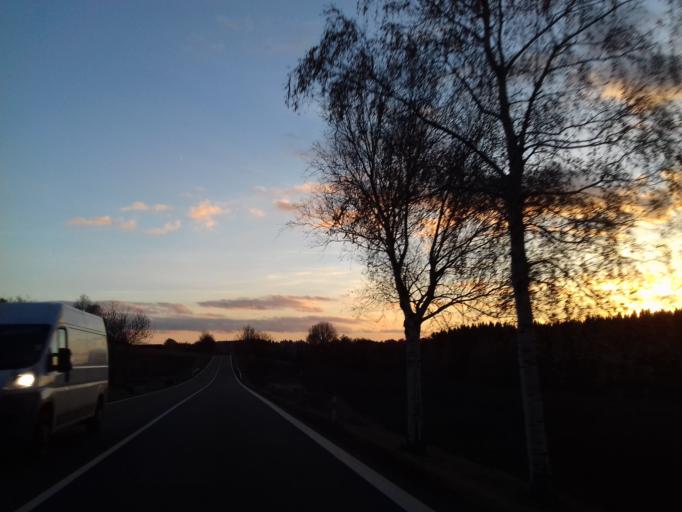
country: CZ
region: Vysocina
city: Krizova
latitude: 49.7226
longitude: 15.8649
